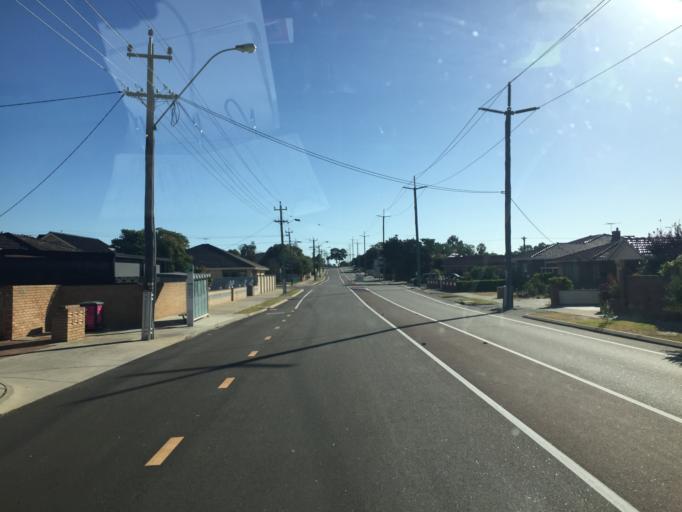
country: AU
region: Western Australia
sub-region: Belmont
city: Rivervale
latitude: -31.9656
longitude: 115.9230
